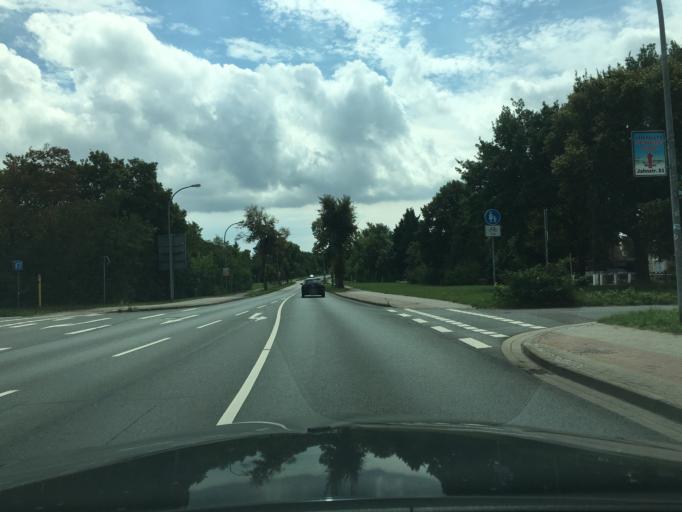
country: DE
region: Saxony-Anhalt
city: Bobbau
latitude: 51.6800
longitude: 12.2742
